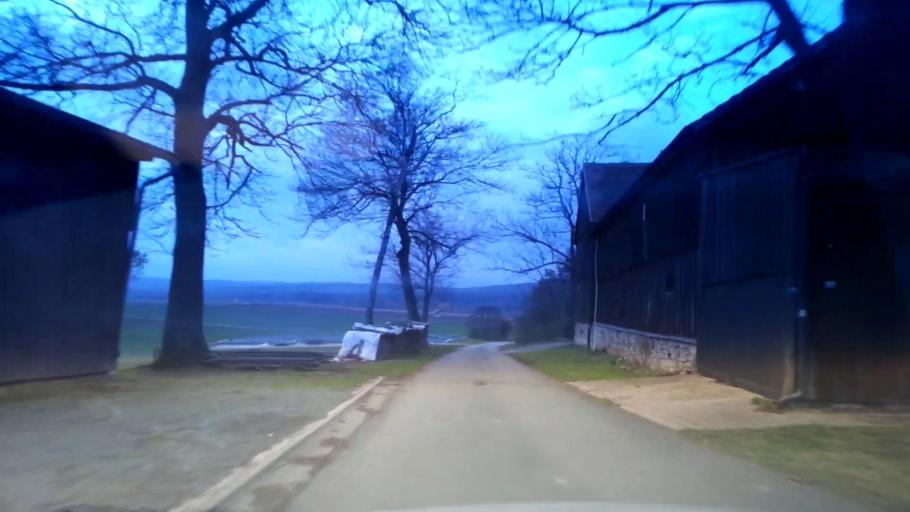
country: DE
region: Bavaria
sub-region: Upper Palatinate
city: Mitterteich
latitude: 49.9436
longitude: 12.2076
